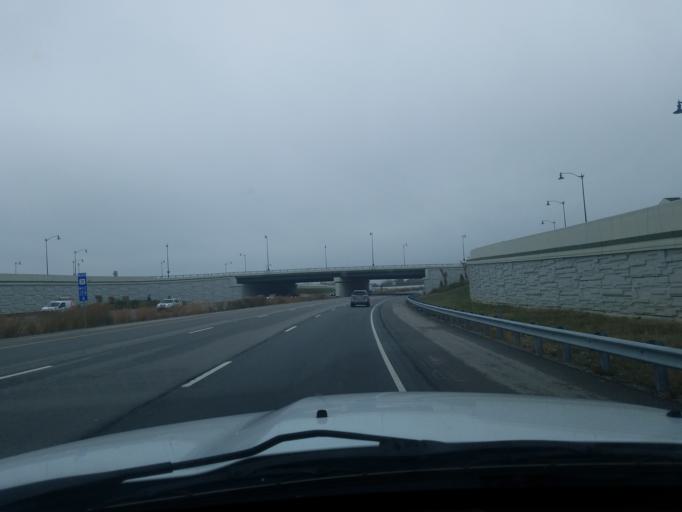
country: US
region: Indiana
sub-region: Hamilton County
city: Carmel
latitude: 39.9762
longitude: -86.1576
